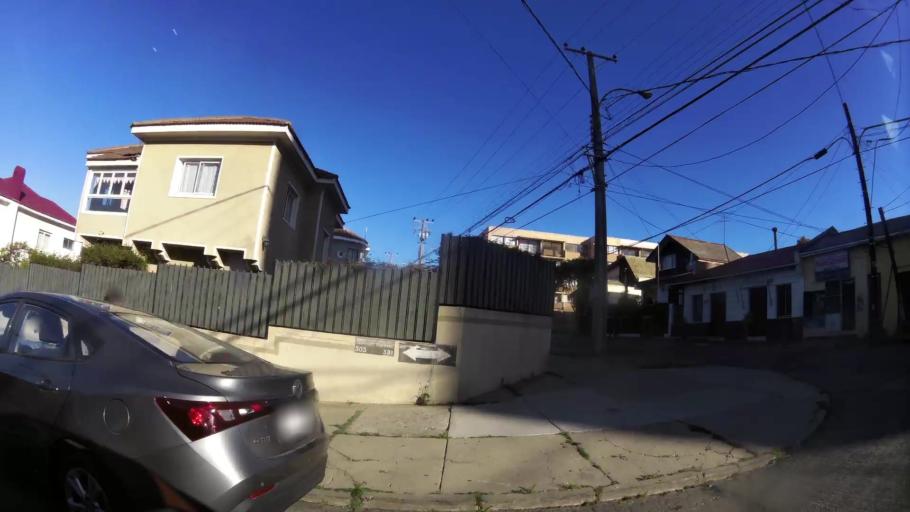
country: CL
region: Valparaiso
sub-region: Provincia de Valparaiso
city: Vina del Mar
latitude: -33.0323
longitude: -71.5801
